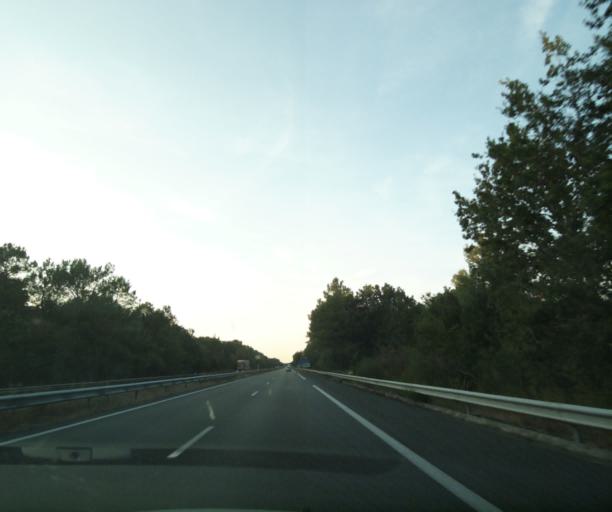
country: FR
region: Aquitaine
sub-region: Departement du Lot-et-Garonne
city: Fourques-sur-Garonne
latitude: 44.3968
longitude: 0.1922
